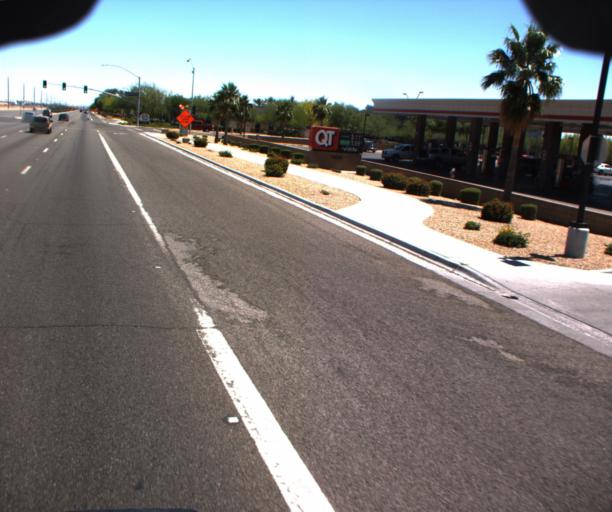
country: US
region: Arizona
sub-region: Maricopa County
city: Sun City West
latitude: 33.6498
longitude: -112.3648
